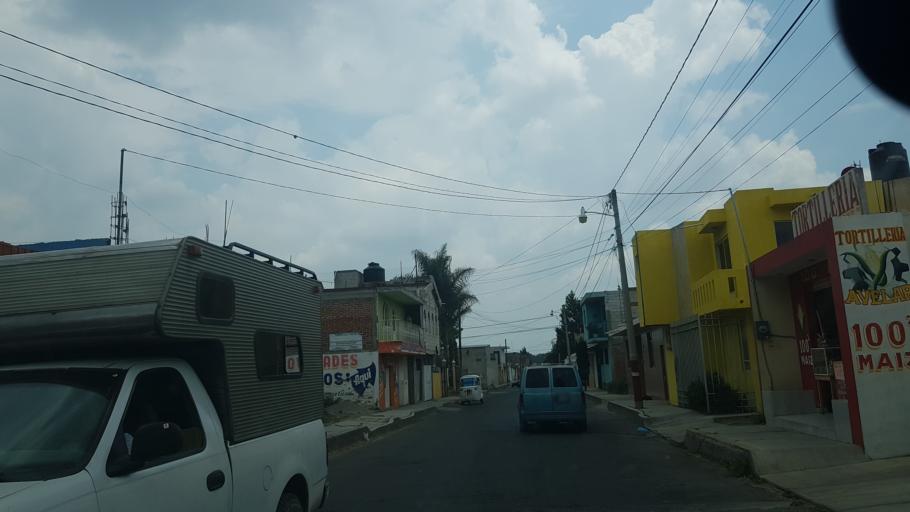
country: MX
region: Puebla
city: Huejotzingo
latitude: 19.1593
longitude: -98.4156
